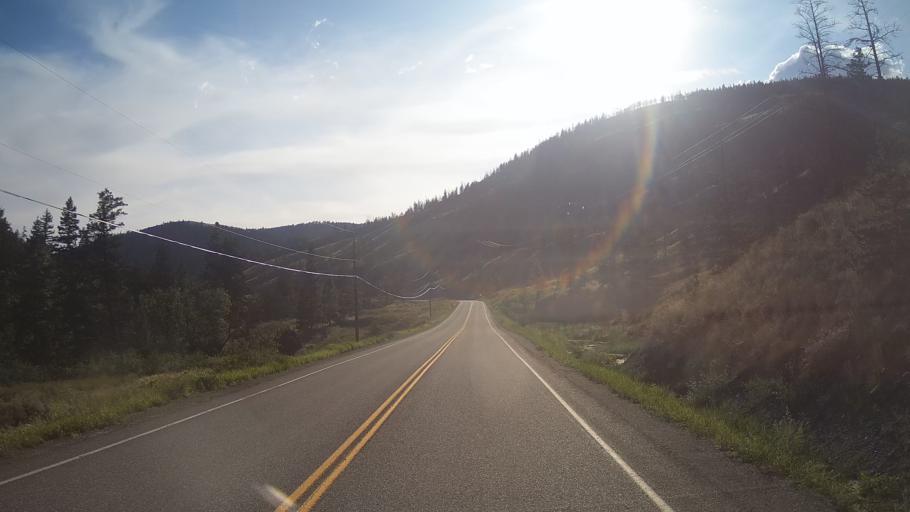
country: CA
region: British Columbia
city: Cache Creek
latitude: 50.8830
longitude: -121.5004
